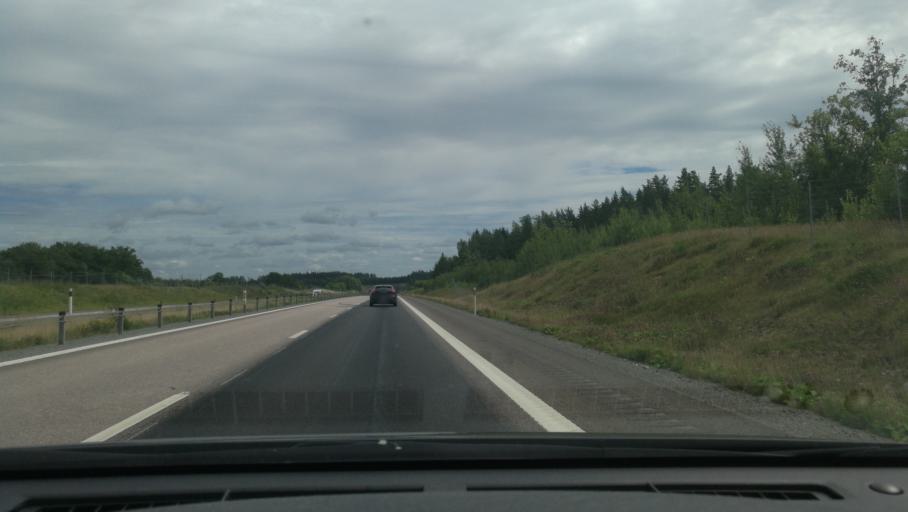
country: SE
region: Uppsala
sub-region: Enkopings Kommun
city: Hummelsta
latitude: 59.6484
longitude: 16.9963
